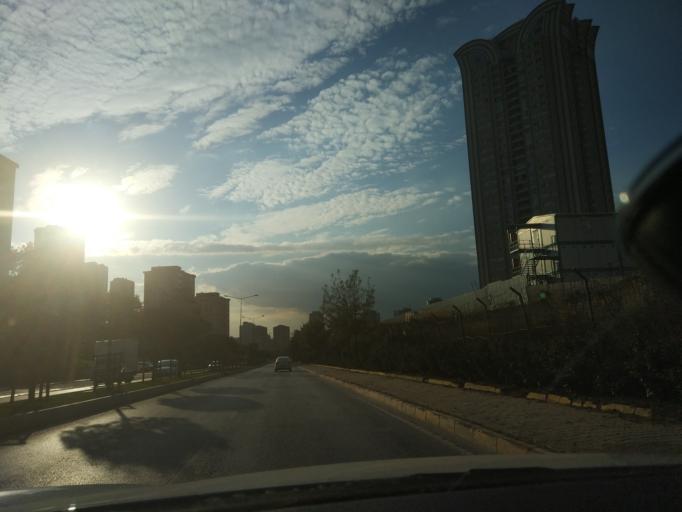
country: TR
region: Istanbul
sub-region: Atasehir
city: Atasehir
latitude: 40.9878
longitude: 29.1194
